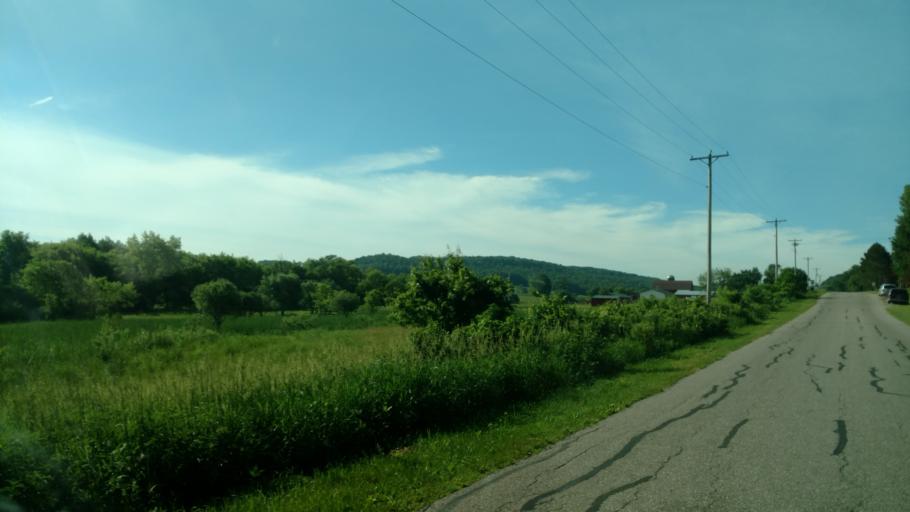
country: US
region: Wisconsin
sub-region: Sauk County
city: Reedsburg
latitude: 43.5495
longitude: -90.1389
